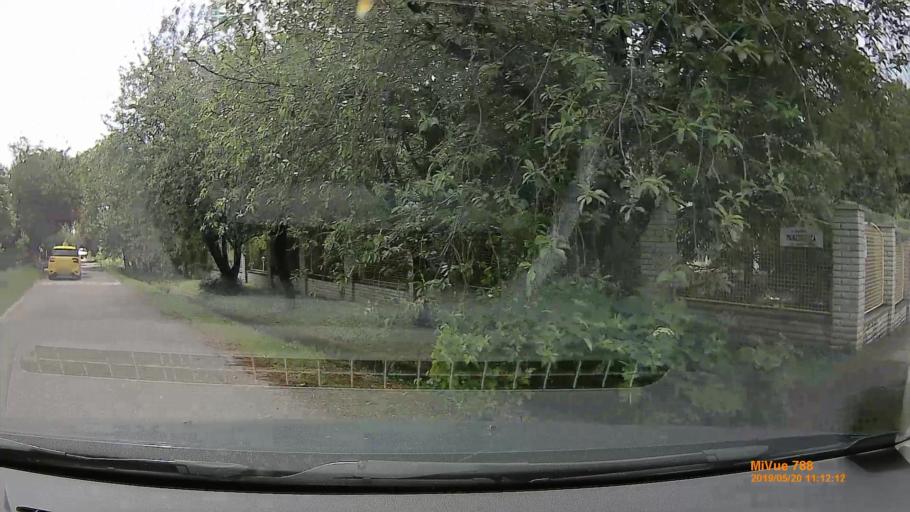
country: HU
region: Pest
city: Ecser
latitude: 47.4630
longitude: 19.2960
